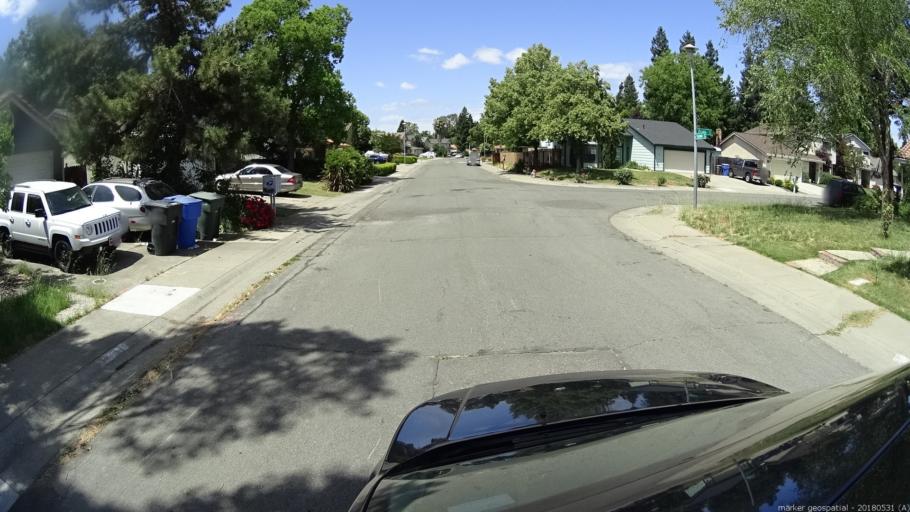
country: US
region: California
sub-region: Sacramento County
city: Sacramento
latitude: 38.6243
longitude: -121.5121
